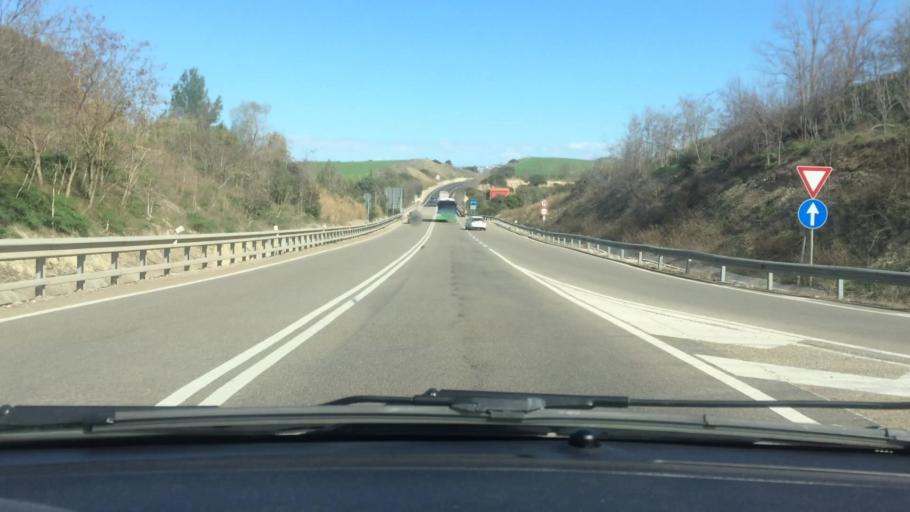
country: IT
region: Basilicate
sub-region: Provincia di Matera
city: La Martella
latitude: 40.5971
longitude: 16.5658
